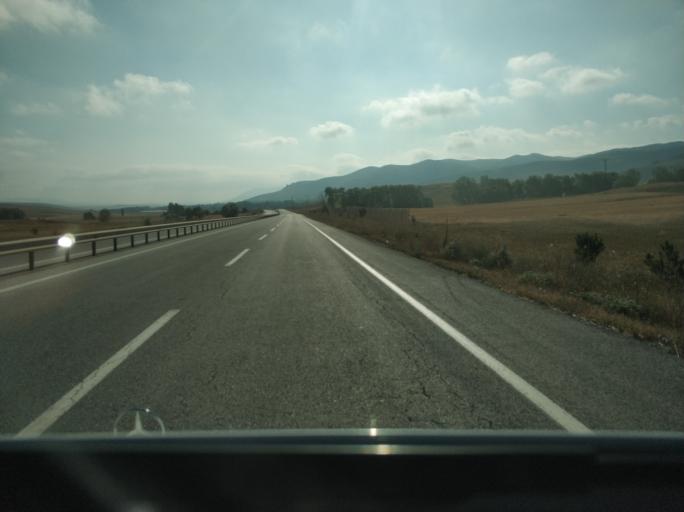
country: TR
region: Sivas
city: Yildizeli
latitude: 39.8355
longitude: 36.4383
